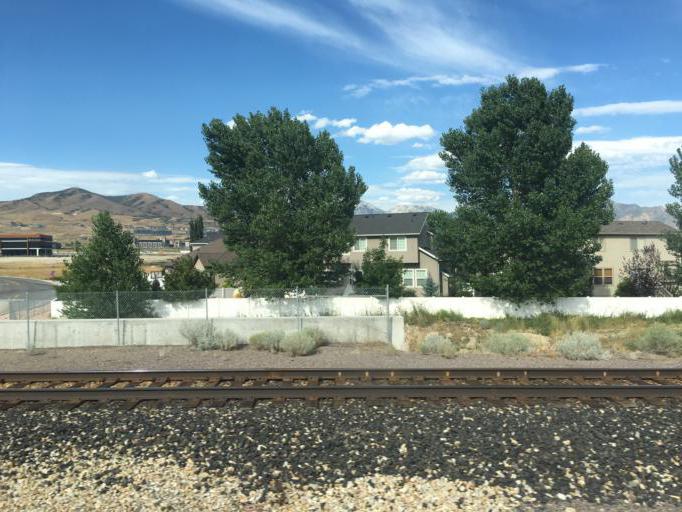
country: US
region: Utah
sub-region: Utah County
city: Lehi
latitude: 40.4160
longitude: -111.8861
